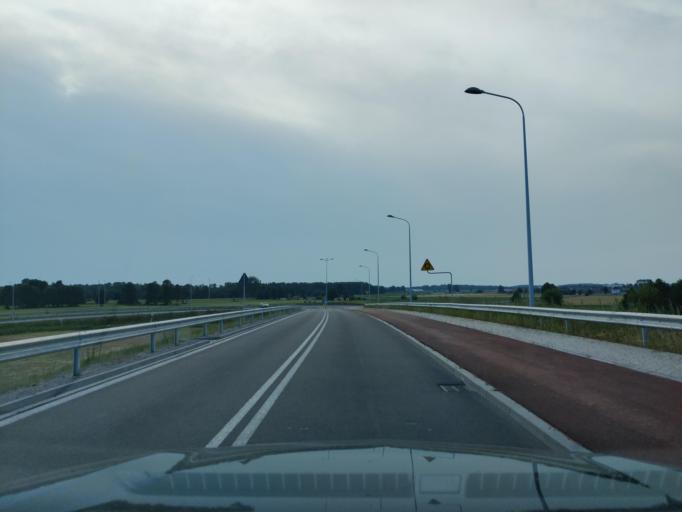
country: PL
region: Masovian Voivodeship
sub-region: Powiat mlawski
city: Strzegowo
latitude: 52.9335
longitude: 20.2867
